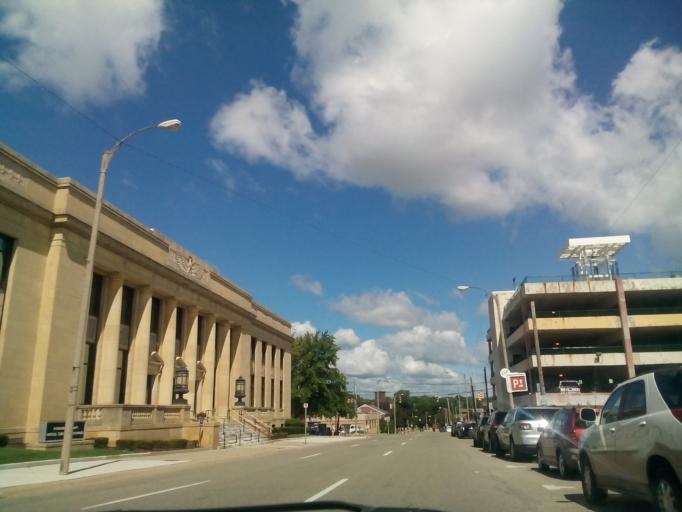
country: US
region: Michigan
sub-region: Genesee County
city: Flint
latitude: 43.0131
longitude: -83.6918
